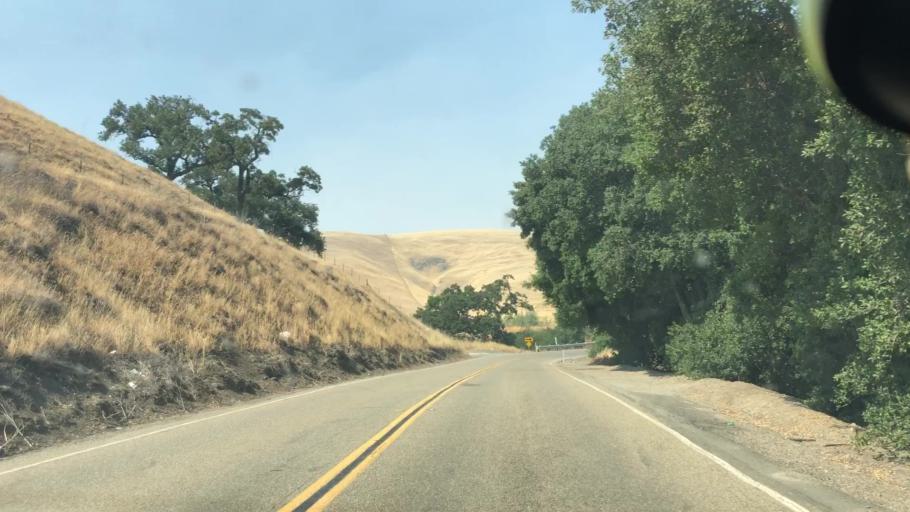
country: US
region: California
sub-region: San Joaquin County
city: Mountain House
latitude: 37.6508
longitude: -121.6149
